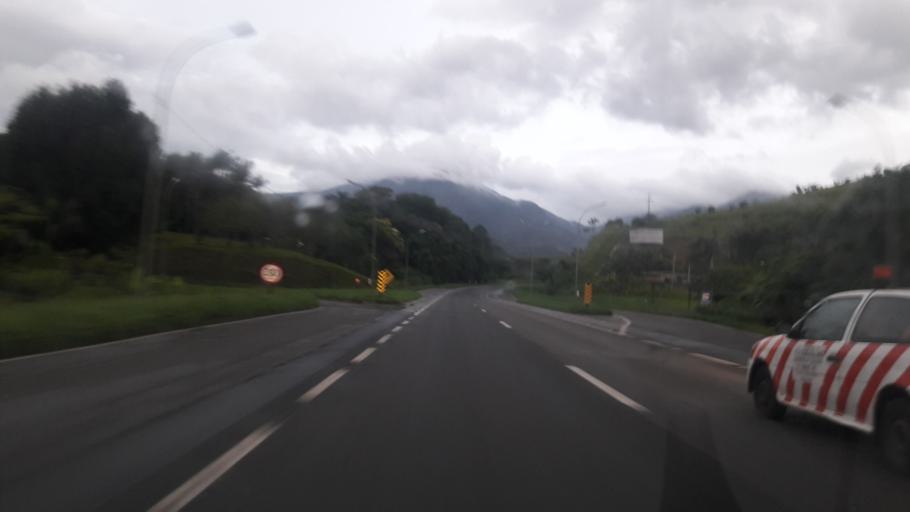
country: BR
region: Sao Paulo
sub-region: Cajati
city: Cajati
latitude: -24.7785
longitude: -48.1969
